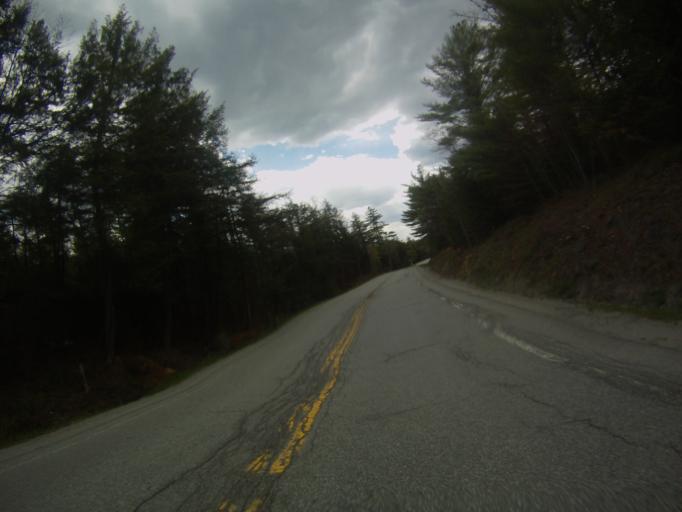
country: US
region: New York
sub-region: Essex County
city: Mineville
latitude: 44.0785
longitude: -73.6006
